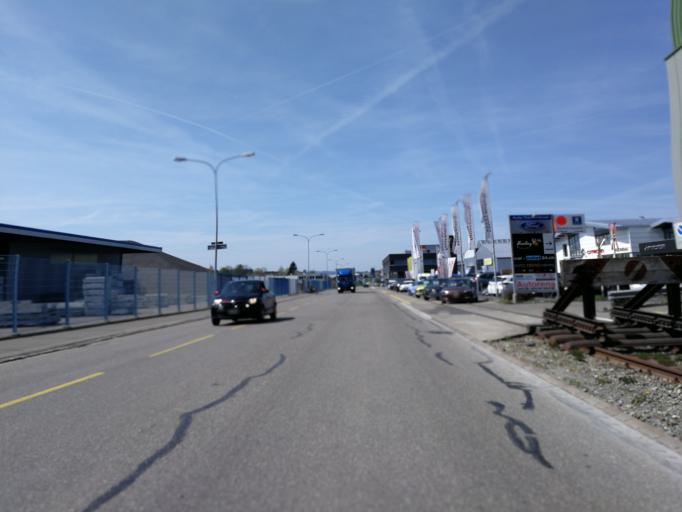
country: CH
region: Zurich
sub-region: Bezirk Hinwil
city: Hinwil
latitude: 47.3038
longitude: 8.8273
